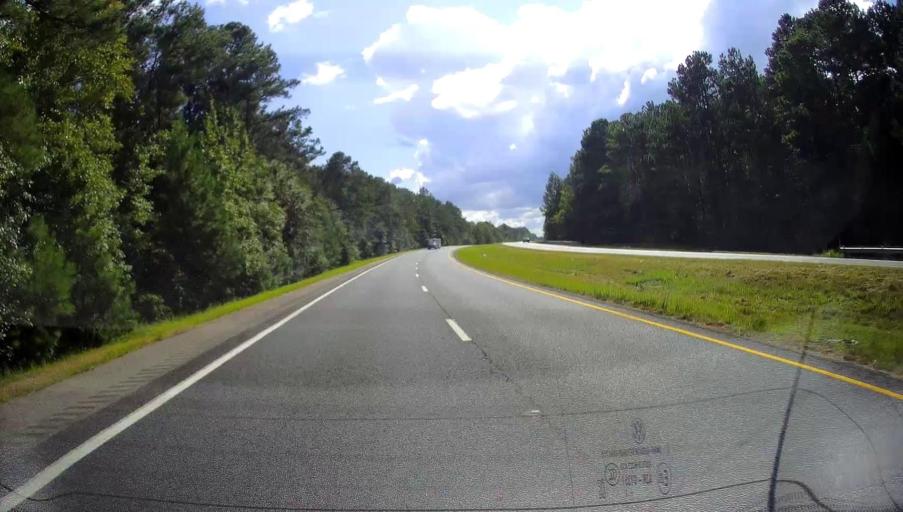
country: US
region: Georgia
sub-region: Muscogee County
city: Columbus
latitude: 32.5628
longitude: -84.8326
